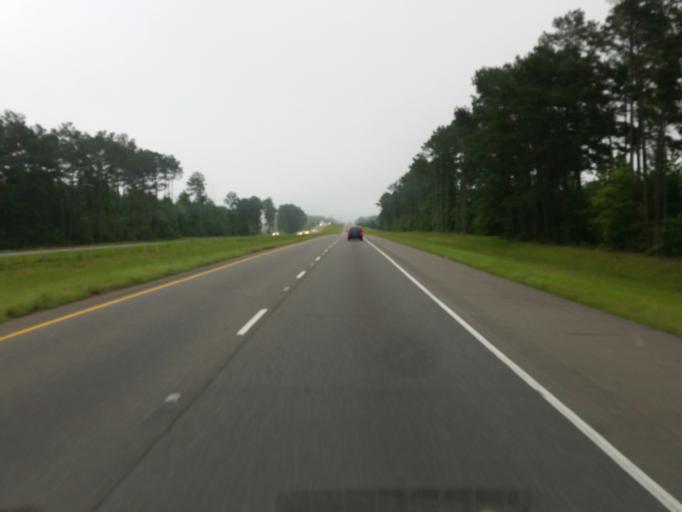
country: US
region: Louisiana
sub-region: Webster Parish
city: Sibley
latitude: 32.5818
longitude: -93.4002
